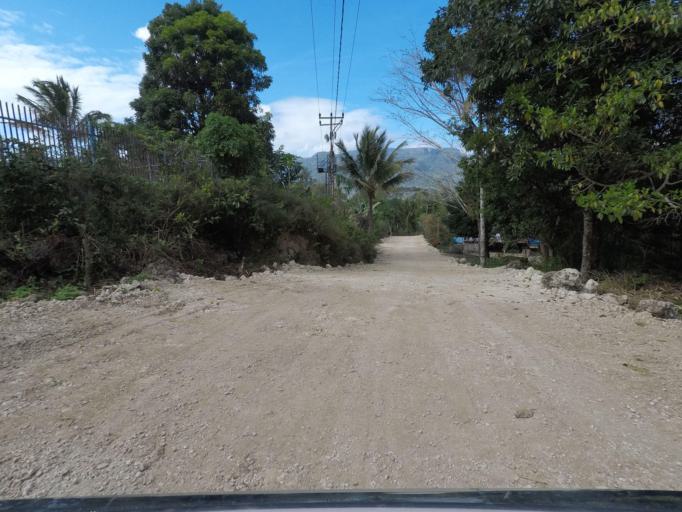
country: TL
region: Baucau
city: Venilale
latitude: -8.6451
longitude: 126.3915
